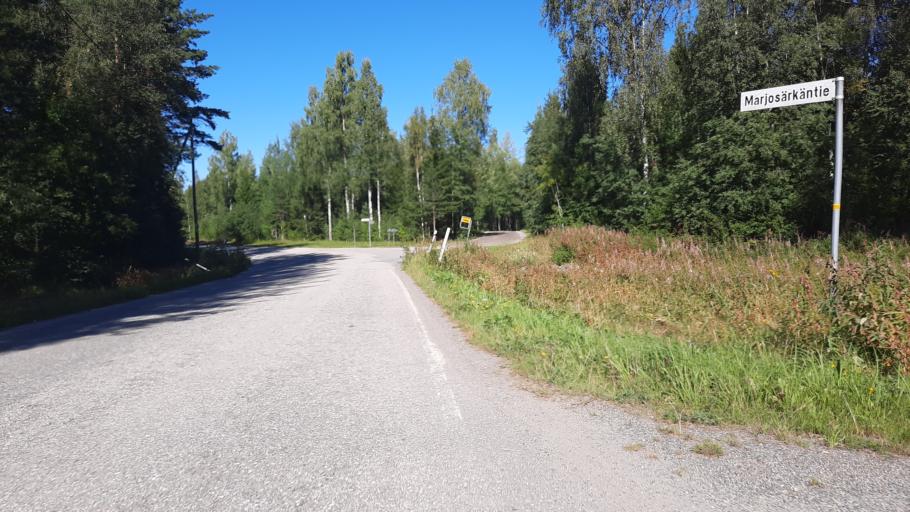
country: FI
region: North Karelia
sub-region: Joensuu
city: Joensuu
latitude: 62.6293
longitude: 29.7357
